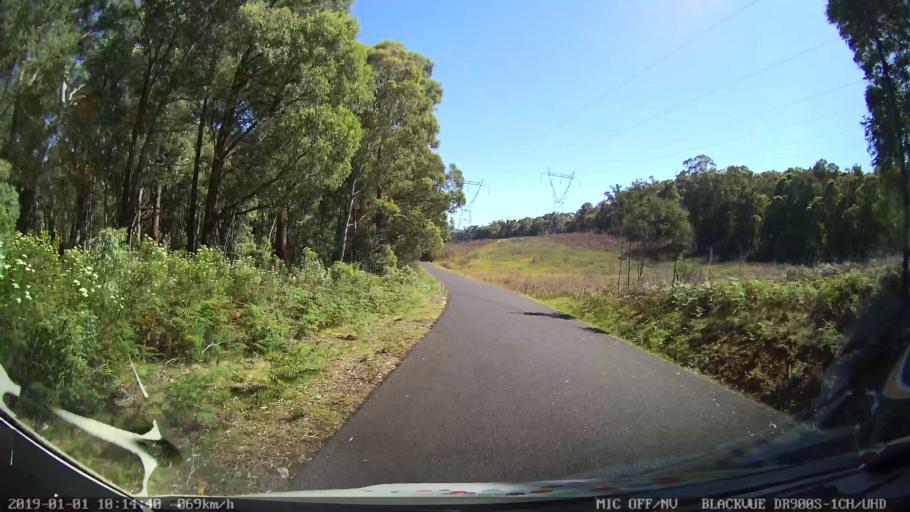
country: AU
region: New South Wales
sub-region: Snowy River
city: Jindabyne
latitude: -36.1101
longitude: 148.1612
